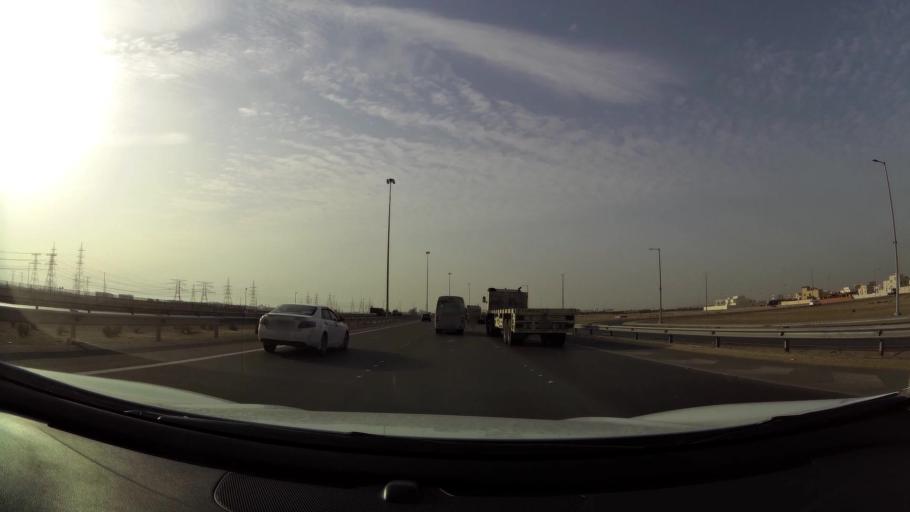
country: AE
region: Abu Dhabi
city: Abu Dhabi
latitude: 24.3052
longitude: 54.5325
